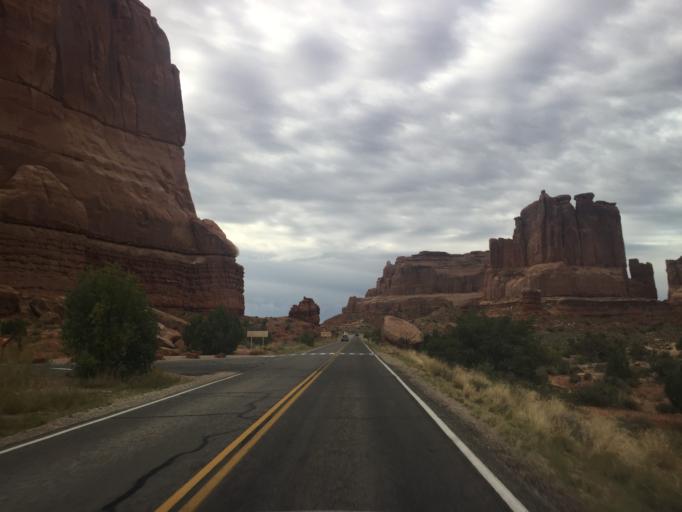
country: US
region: Utah
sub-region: Grand County
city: Moab
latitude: 38.6372
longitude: -109.6004
